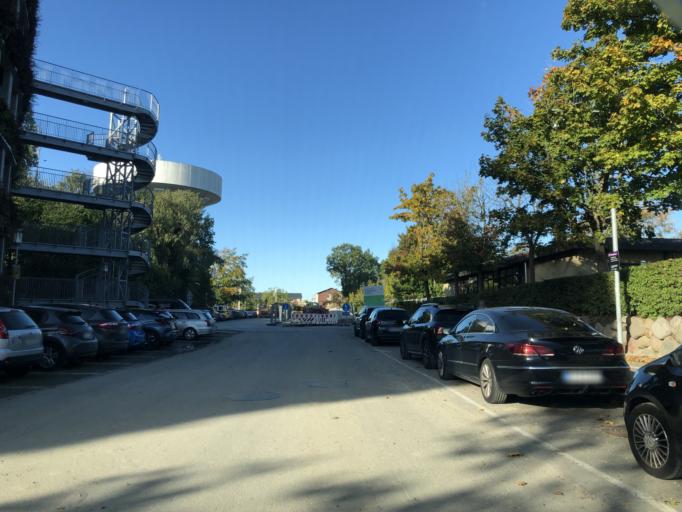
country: DK
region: Capital Region
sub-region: Glostrup Kommune
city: Glostrup
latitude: 55.6720
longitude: 12.3871
